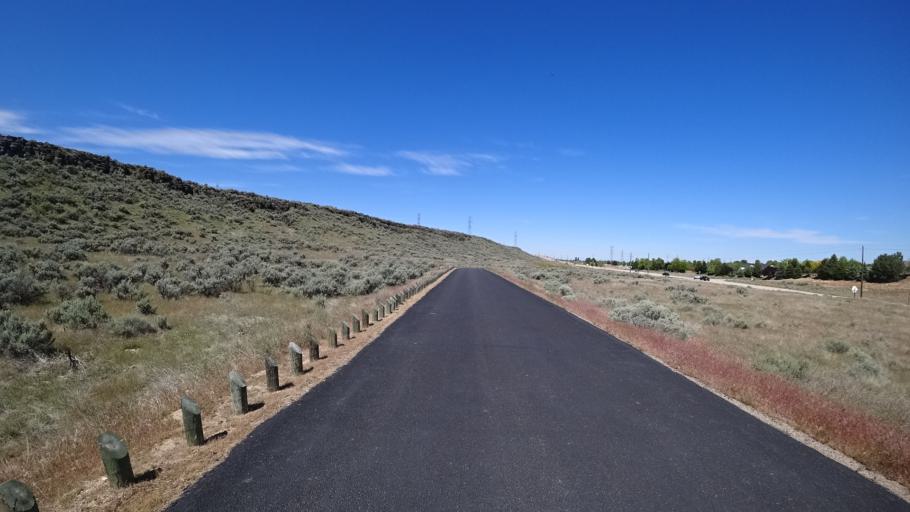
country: US
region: Idaho
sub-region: Ada County
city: Boise
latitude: 43.5424
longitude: -116.1125
